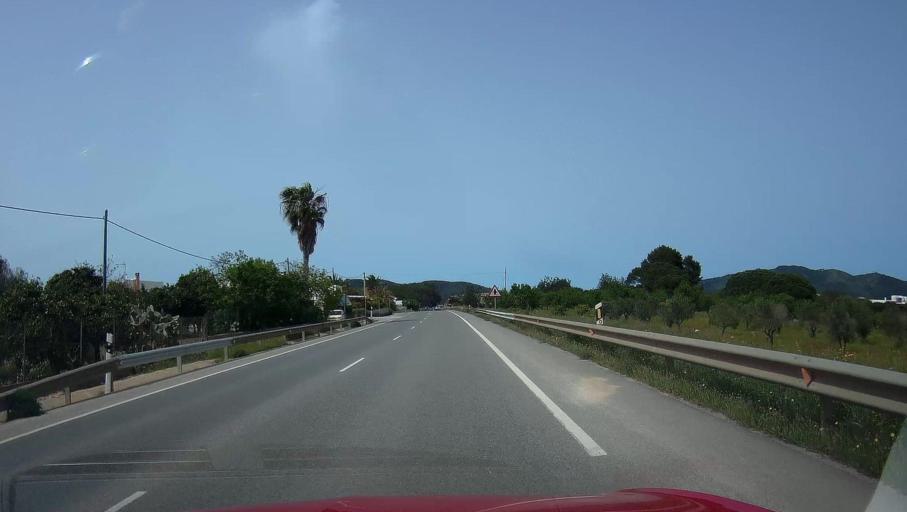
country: ES
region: Balearic Islands
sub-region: Illes Balears
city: Santa Eularia des Riu
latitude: 39.0113
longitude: 1.4879
